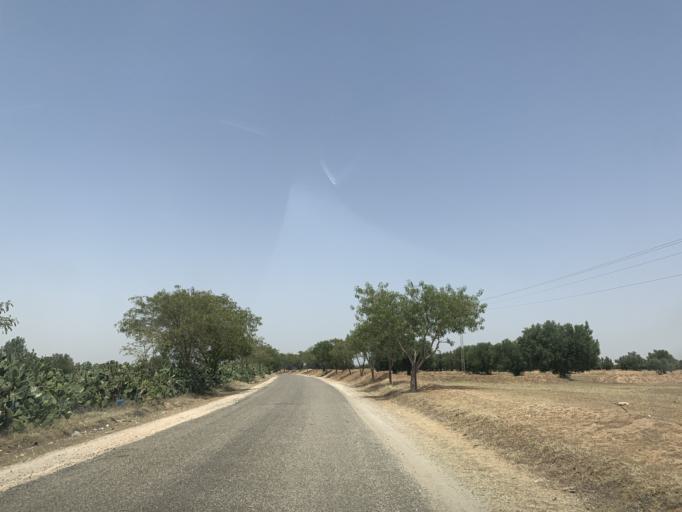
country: TN
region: Al Mahdiyah
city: Shurban
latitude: 35.1828
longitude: 10.2397
